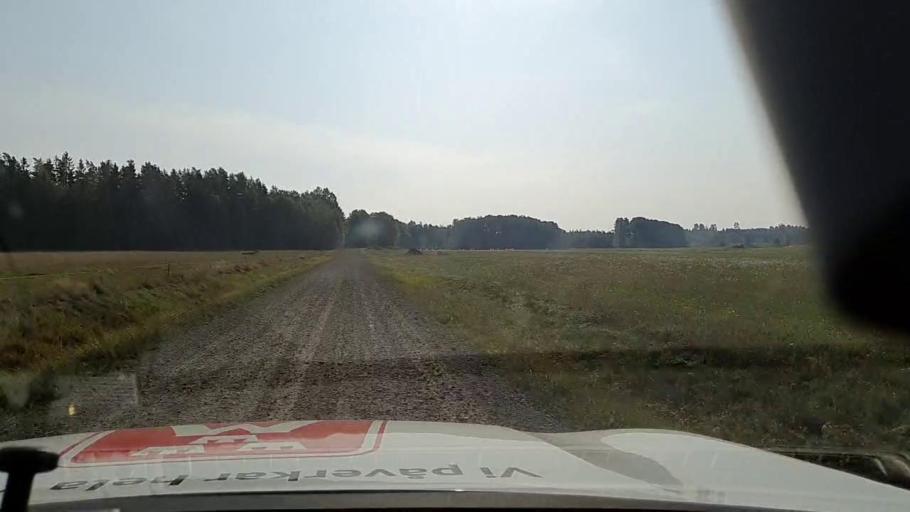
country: SE
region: Vaestmanland
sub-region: Kungsors Kommun
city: Kungsoer
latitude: 59.3524
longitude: 16.1620
